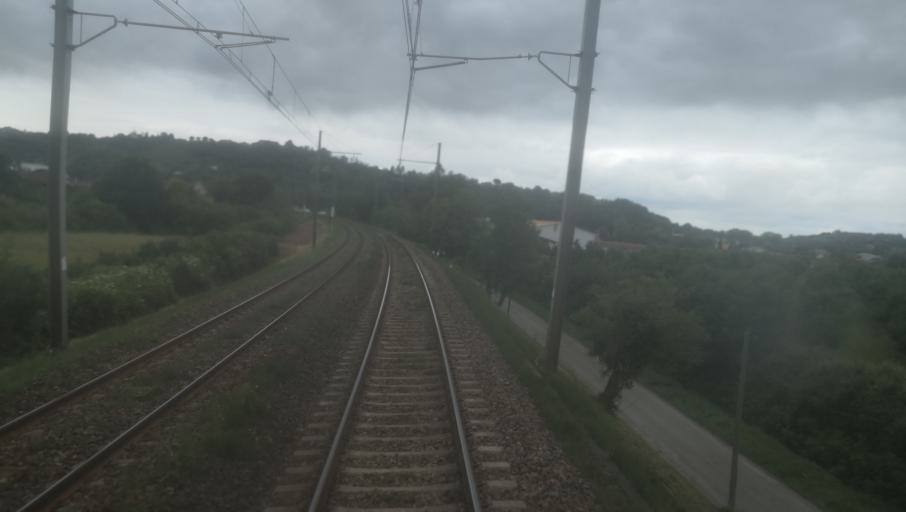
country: FR
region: Midi-Pyrenees
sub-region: Departement du Tarn-et-Garonne
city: Moissac
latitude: 44.1012
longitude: 1.1053
